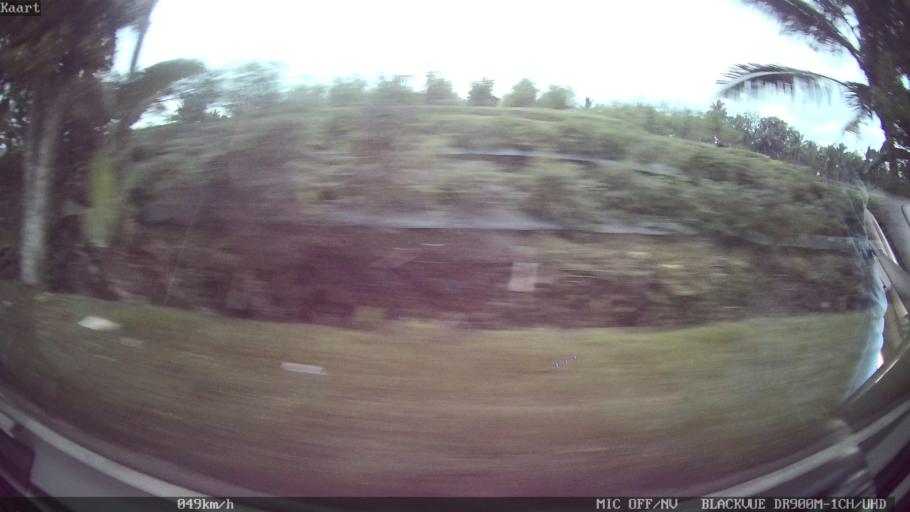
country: ID
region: Bali
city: Empalan
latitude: -8.4063
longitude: 115.1465
